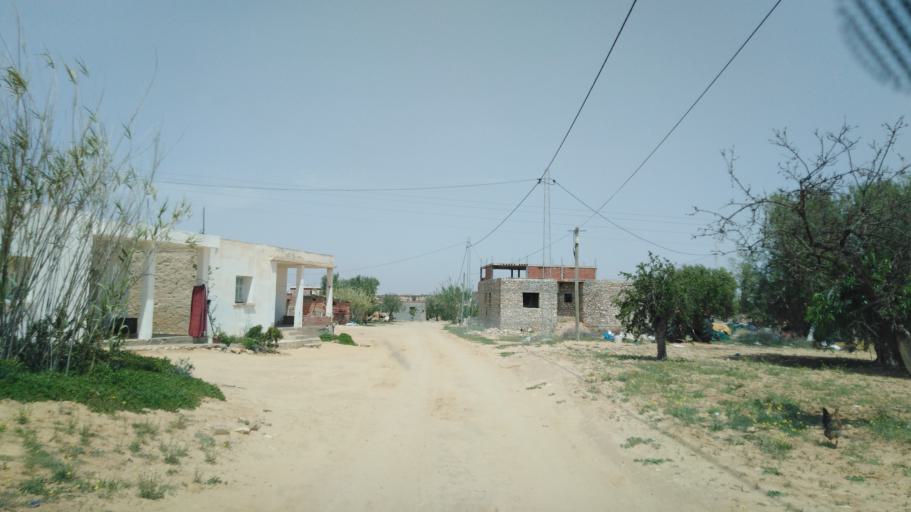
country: TN
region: Safaqis
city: Sfax
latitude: 34.7300
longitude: 10.5541
